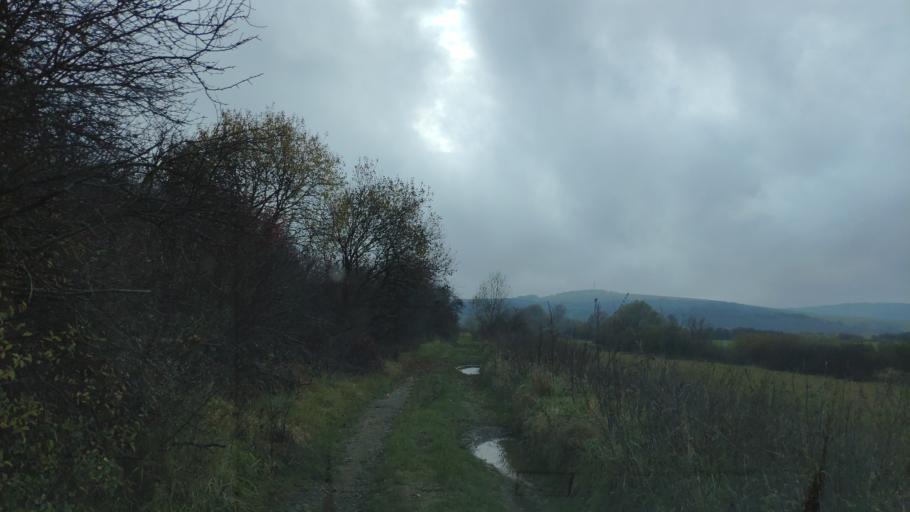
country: SK
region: Presovsky
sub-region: Okres Presov
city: Presov
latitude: 49.0219
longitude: 21.1991
